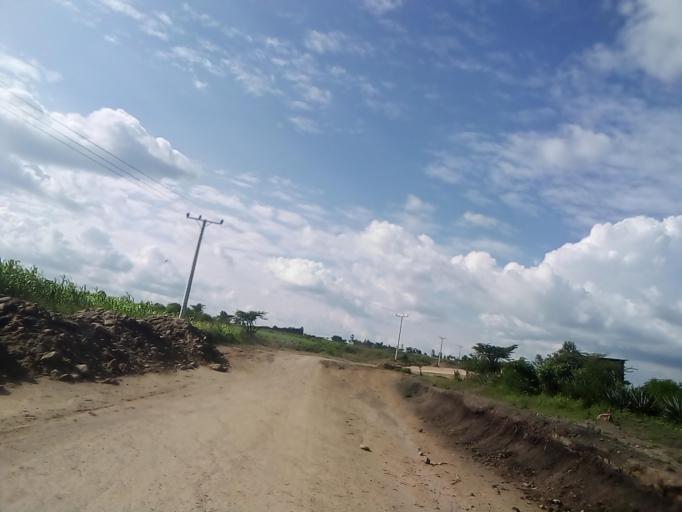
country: ET
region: Southern Nations, Nationalities, and People's Region
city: K'olito
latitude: 7.6258
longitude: 38.0639
